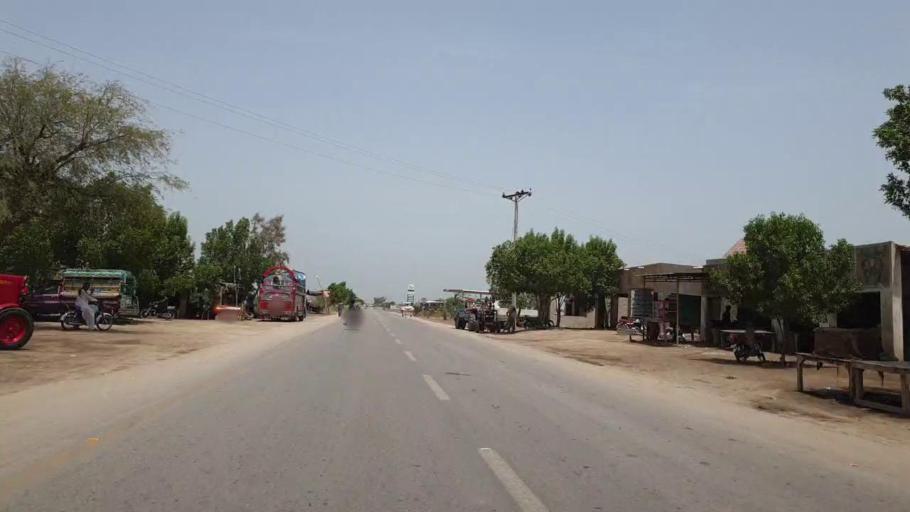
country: PK
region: Sindh
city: Nawabshah
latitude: 26.2224
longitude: 68.4973
